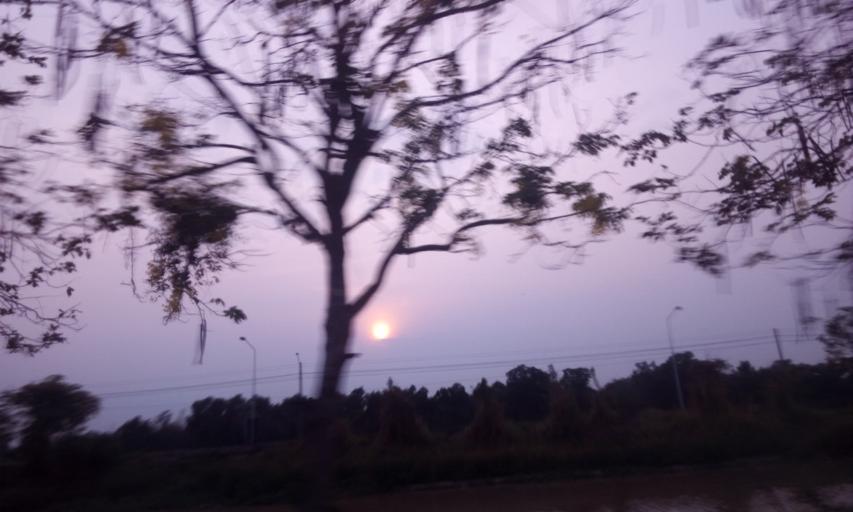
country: TH
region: Bangkok
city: Nong Chok
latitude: 13.9646
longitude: 100.8955
